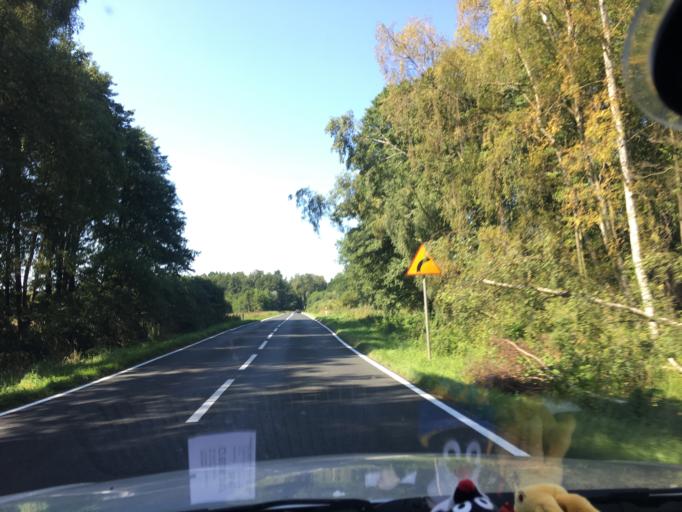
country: PL
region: West Pomeranian Voivodeship
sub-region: Powiat gryficki
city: Pobierowo
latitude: 54.0401
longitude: 14.8624
